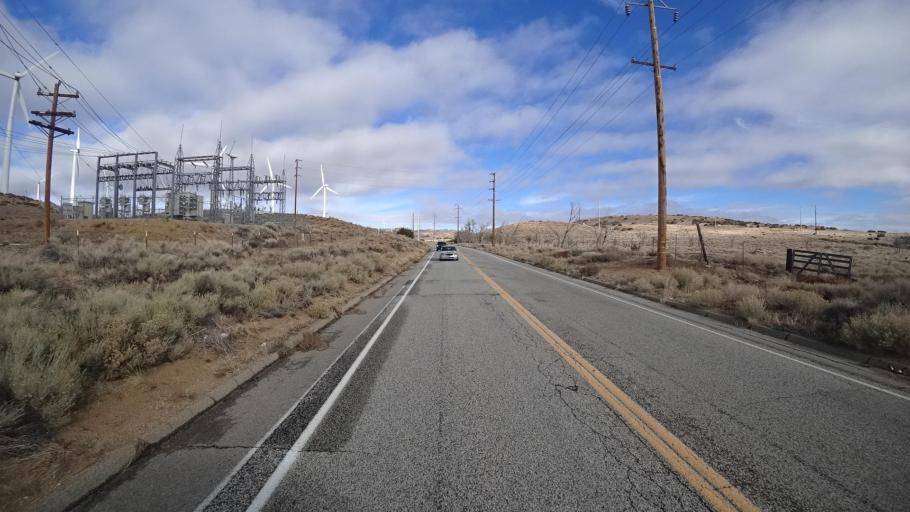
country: US
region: California
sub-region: Kern County
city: Tehachapi
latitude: 35.0345
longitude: -118.3513
